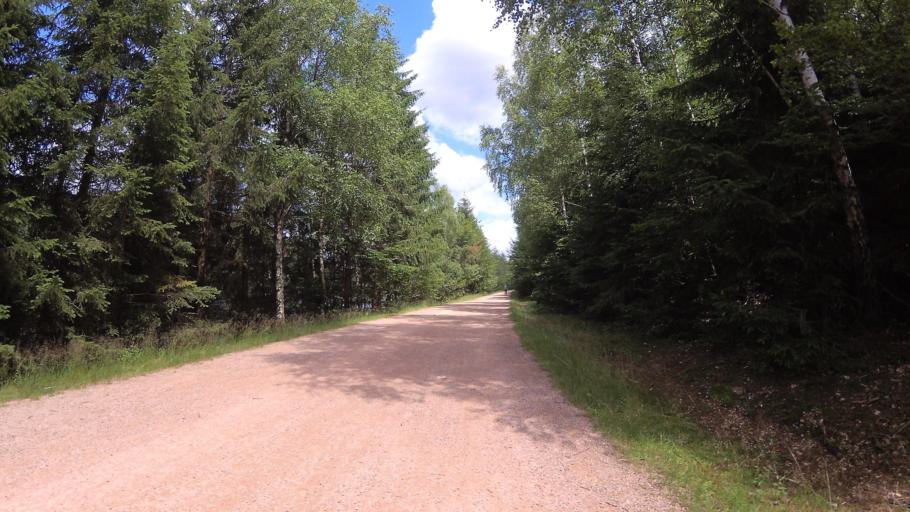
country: DE
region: Saarland
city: Nonnweiler
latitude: 49.6155
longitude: 6.9827
